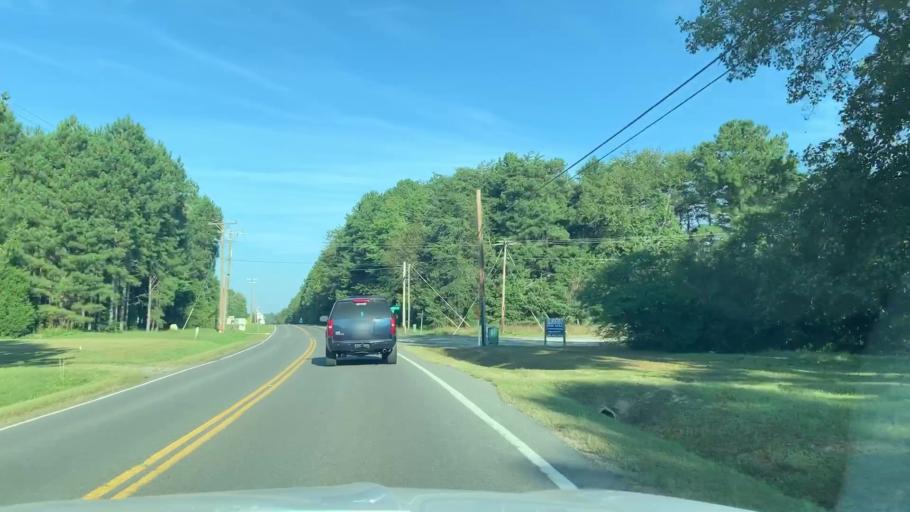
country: US
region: Virginia
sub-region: Lancaster County
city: Lancaster
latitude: 37.7636
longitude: -76.4240
